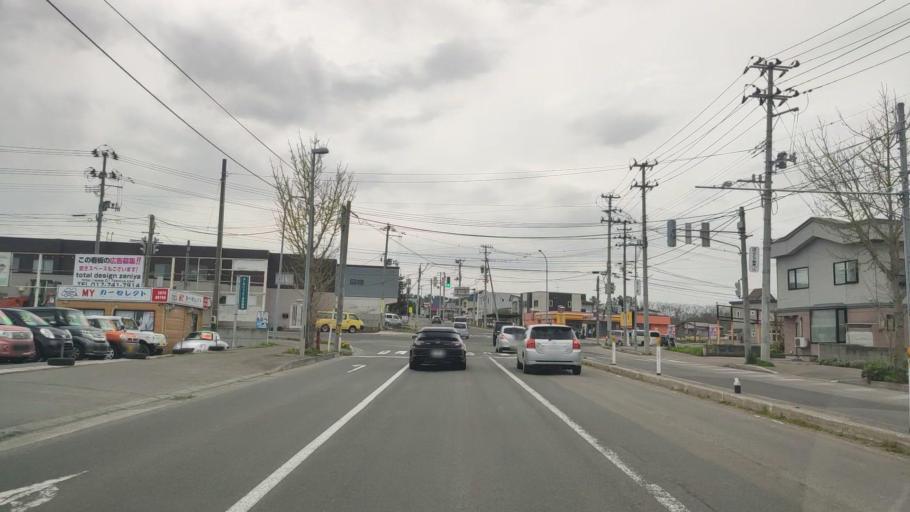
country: JP
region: Aomori
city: Aomori Shi
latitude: 40.7902
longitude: 140.7870
